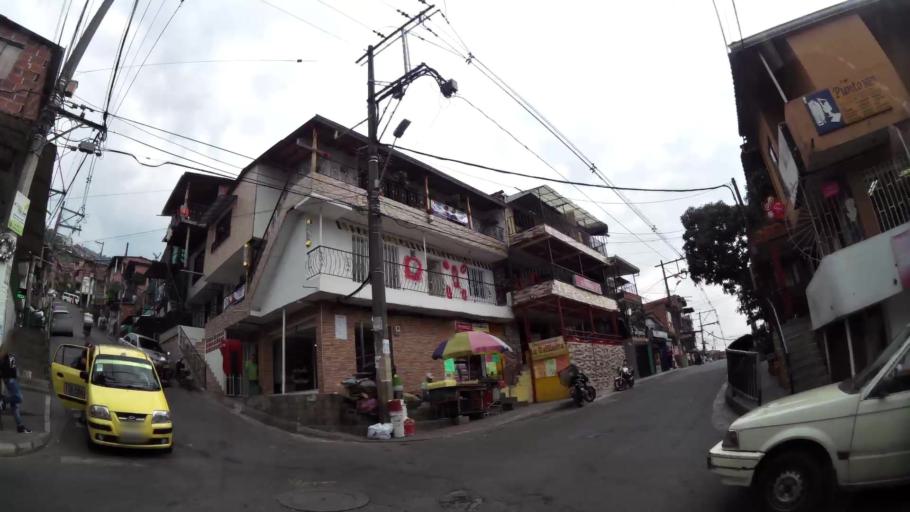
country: CO
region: Antioquia
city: Bello
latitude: 6.2997
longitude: -75.5493
